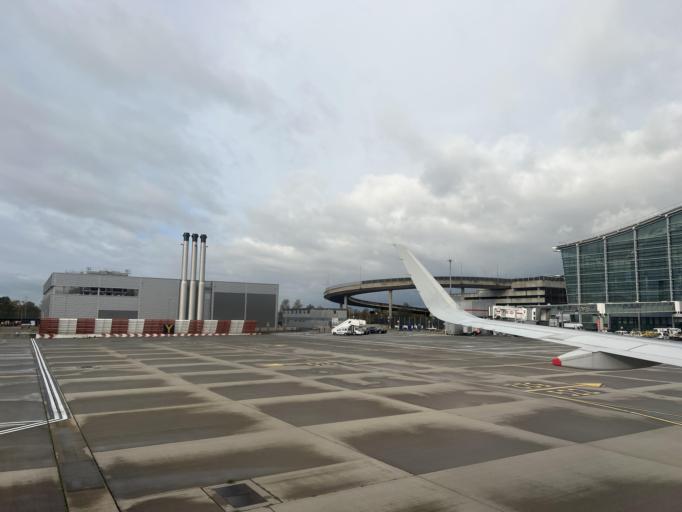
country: GB
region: England
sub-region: Buckinghamshire
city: Iver
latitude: 51.4685
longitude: -0.4876
